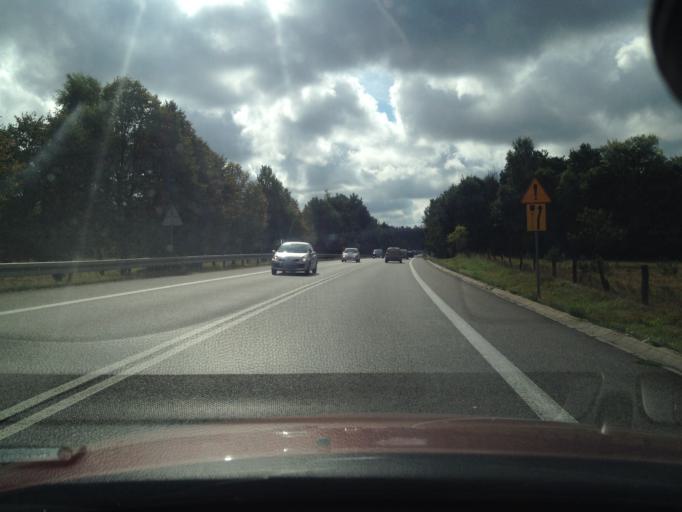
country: PL
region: West Pomeranian Voivodeship
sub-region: Powiat goleniowski
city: Przybiernow
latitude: 53.6815
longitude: 14.8088
